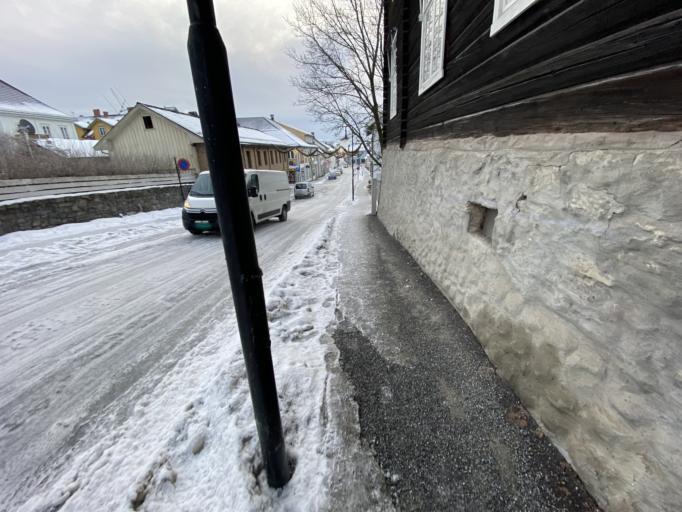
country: NO
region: Buskerud
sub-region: Kongsberg
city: Kongsberg
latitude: 59.6646
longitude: 9.6458
